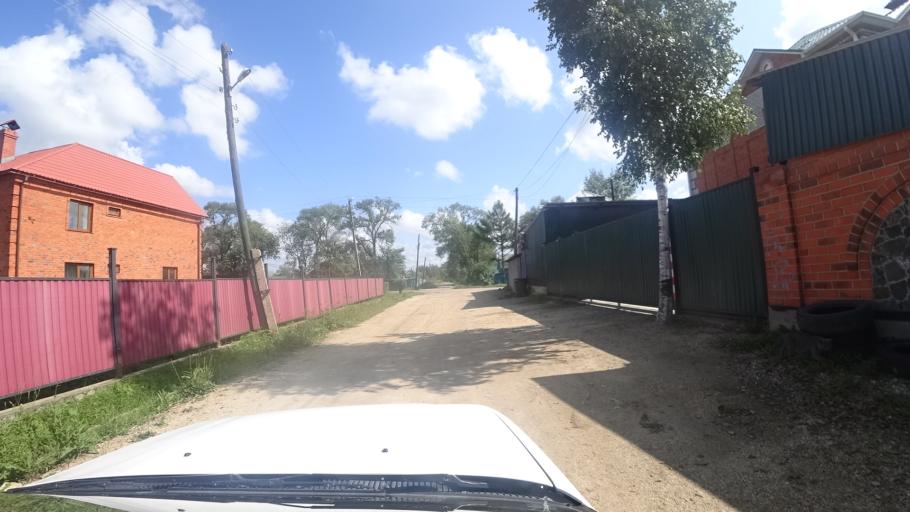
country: RU
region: Primorskiy
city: Dal'nerechensk
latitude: 45.9242
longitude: 133.7184
